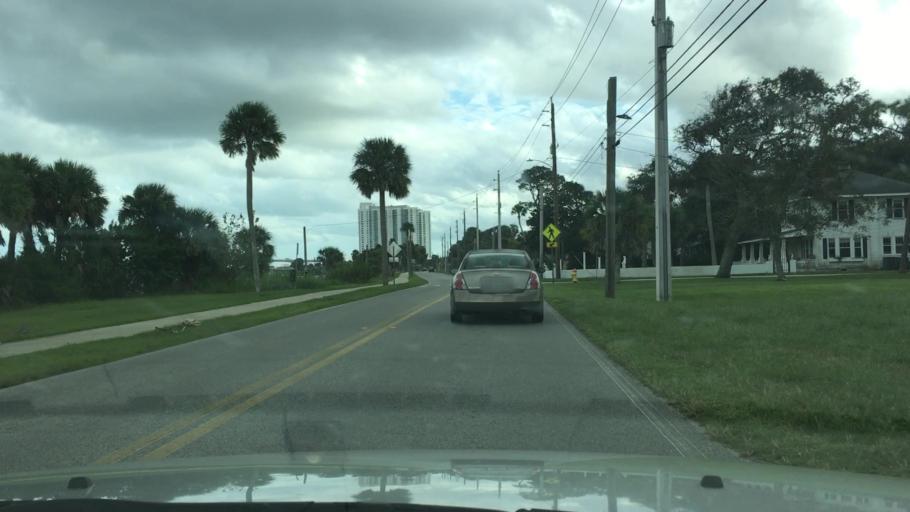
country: US
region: Florida
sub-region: Volusia County
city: Holly Hill
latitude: 29.2413
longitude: -81.0347
